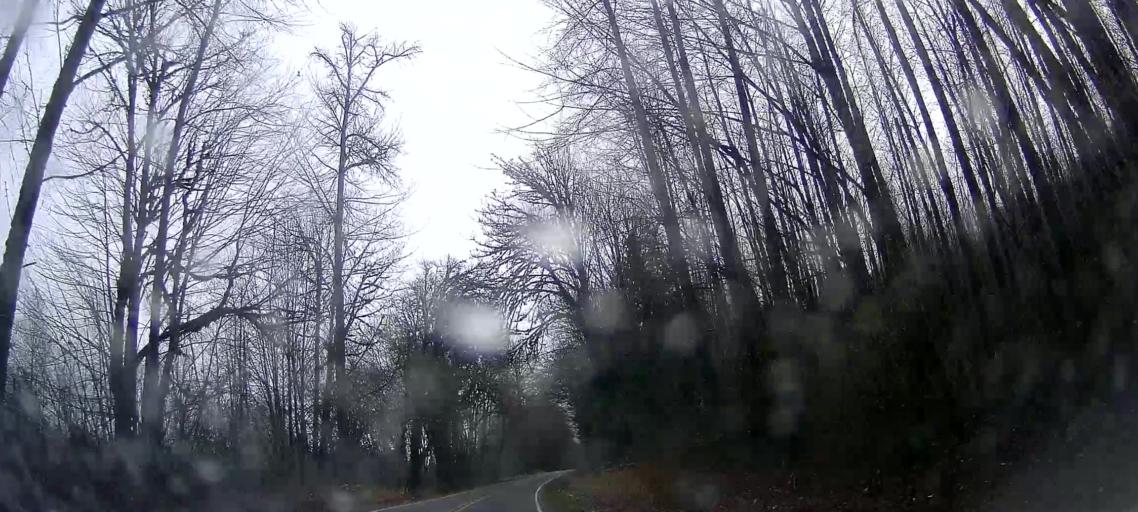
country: US
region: Washington
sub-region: Snohomish County
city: Darrington
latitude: 48.5315
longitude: -121.7890
